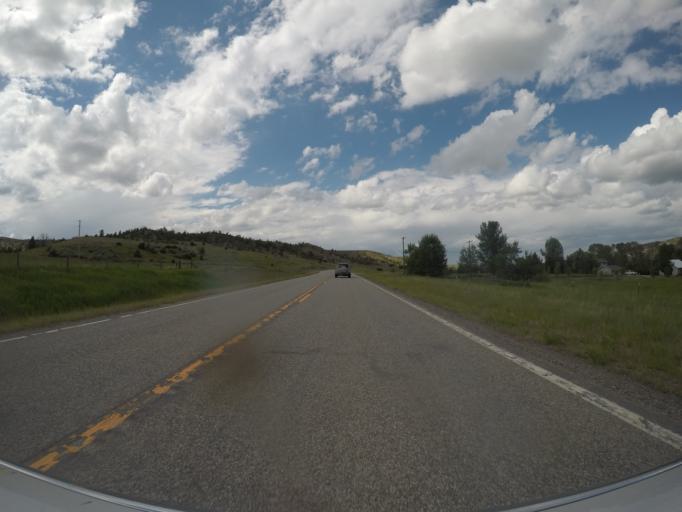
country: US
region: Montana
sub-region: Sweet Grass County
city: Big Timber
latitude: 45.7262
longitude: -109.9974
